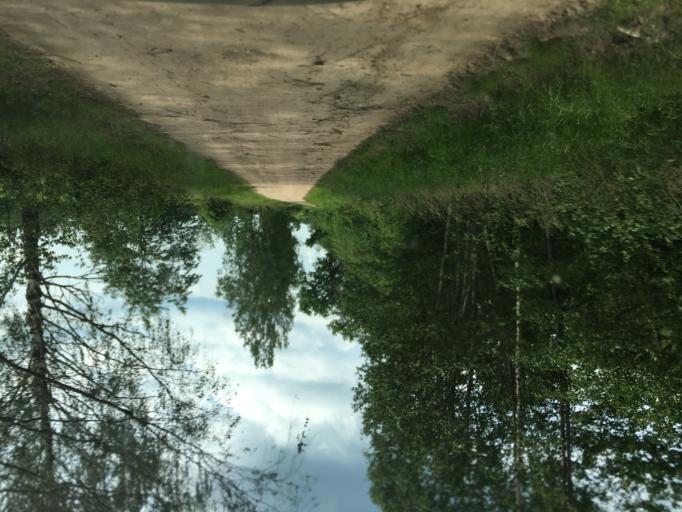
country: LV
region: Rugaju
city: Rugaji
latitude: 56.9750
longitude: 27.0568
